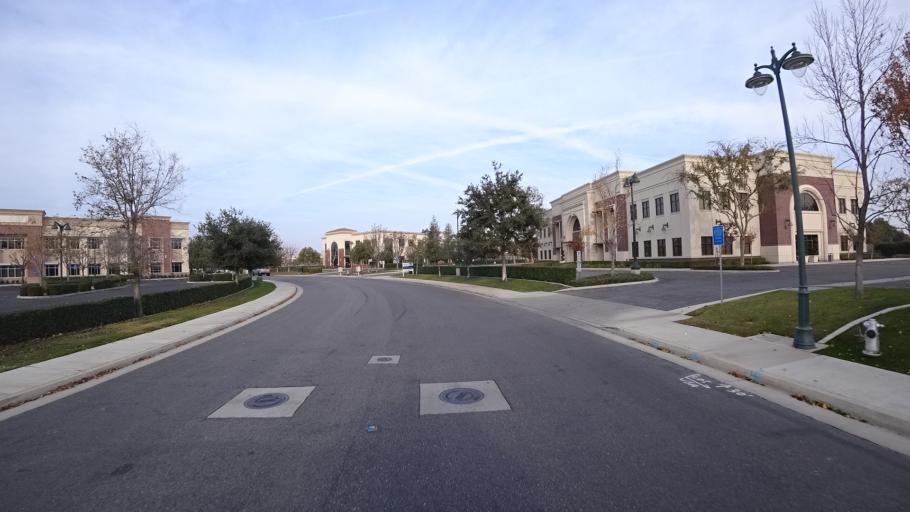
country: US
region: California
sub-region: Kern County
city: Greenacres
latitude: 35.3474
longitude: -119.1252
